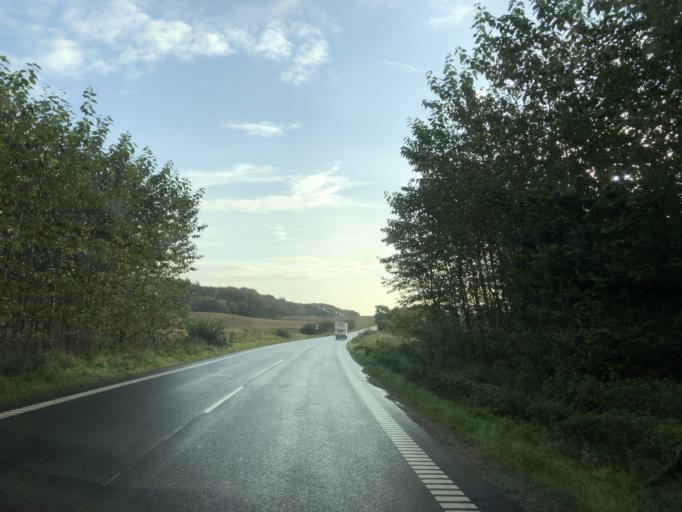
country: DK
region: North Denmark
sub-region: Mariagerfjord Kommune
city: Hobro
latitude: 56.6156
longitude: 9.6701
